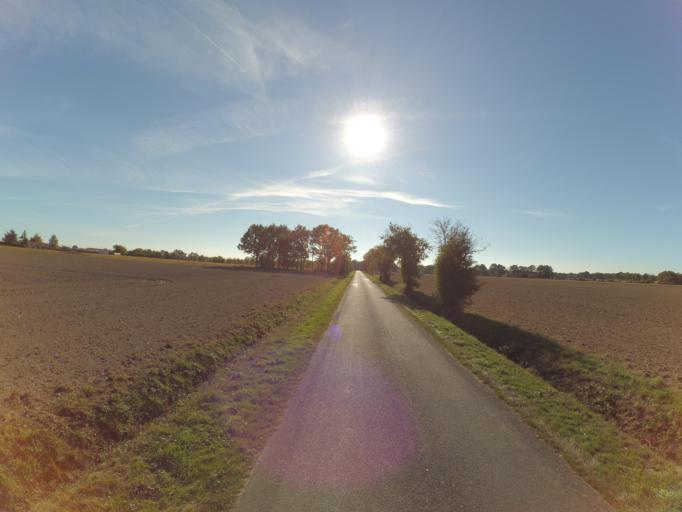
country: FR
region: Pays de la Loire
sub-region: Departement de la Loire-Atlantique
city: Saint-Lumine-de-Clisson
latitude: 47.0687
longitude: -1.3347
